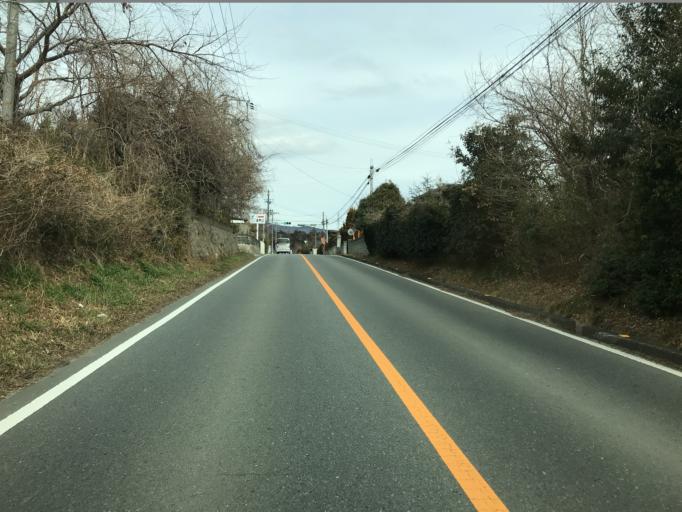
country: JP
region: Fukushima
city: Iwaki
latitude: 37.0990
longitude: 140.8743
